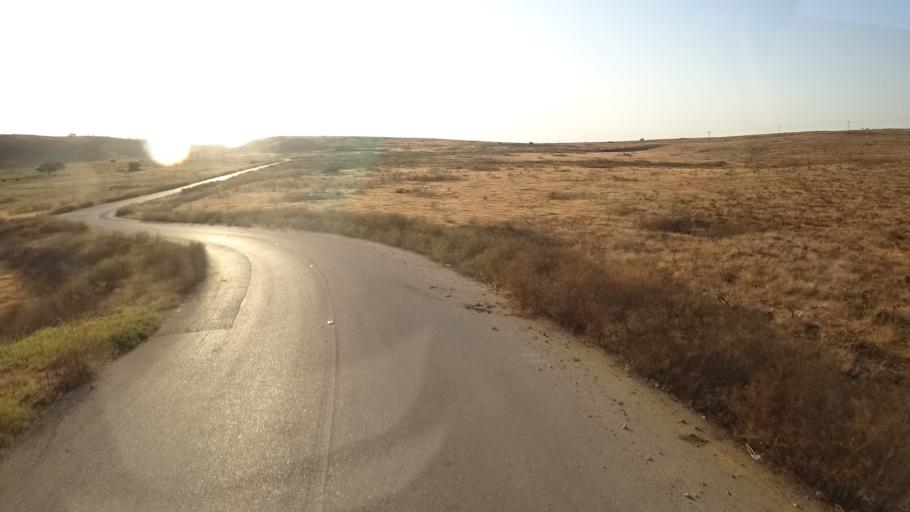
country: OM
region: Zufar
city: Salalah
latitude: 17.1549
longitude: 54.6215
